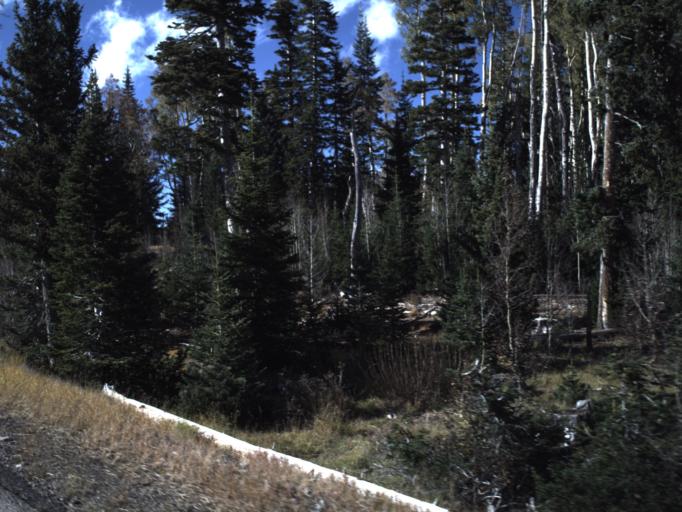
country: US
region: Utah
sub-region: Iron County
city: Parowan
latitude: 37.6523
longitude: -112.7996
